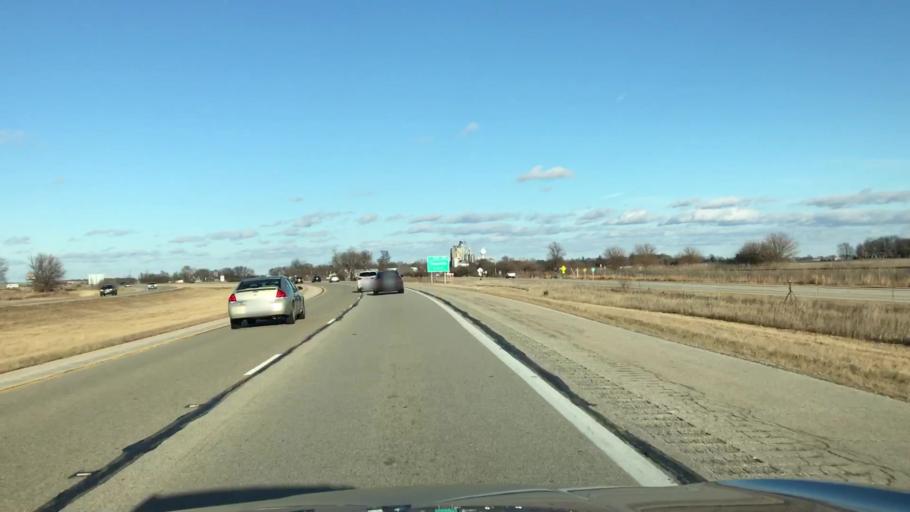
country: US
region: Illinois
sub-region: McLean County
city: Normal
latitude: 40.5556
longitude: -88.9124
